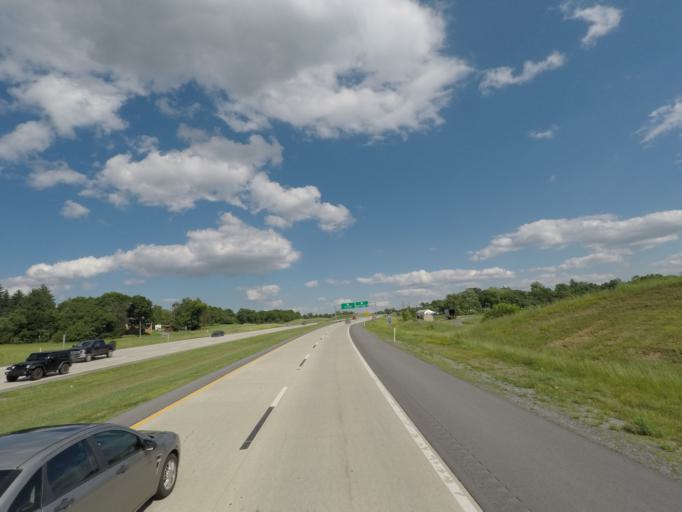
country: US
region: West Virginia
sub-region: Berkeley County
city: Martinsburg
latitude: 39.4226
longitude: -77.9332
